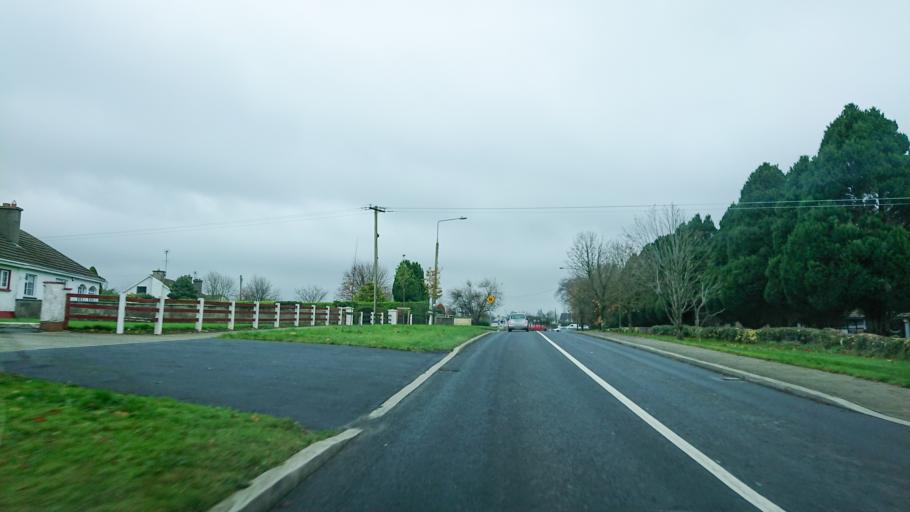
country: IE
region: Leinster
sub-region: Kilkenny
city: Mooncoin
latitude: 52.2970
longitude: -7.2626
